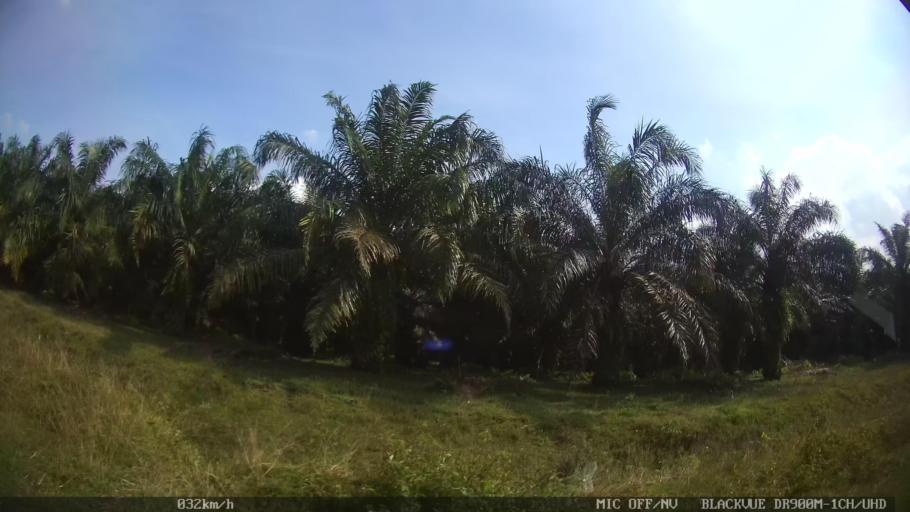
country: ID
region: North Sumatra
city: Binjai
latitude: 3.6425
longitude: 98.5296
